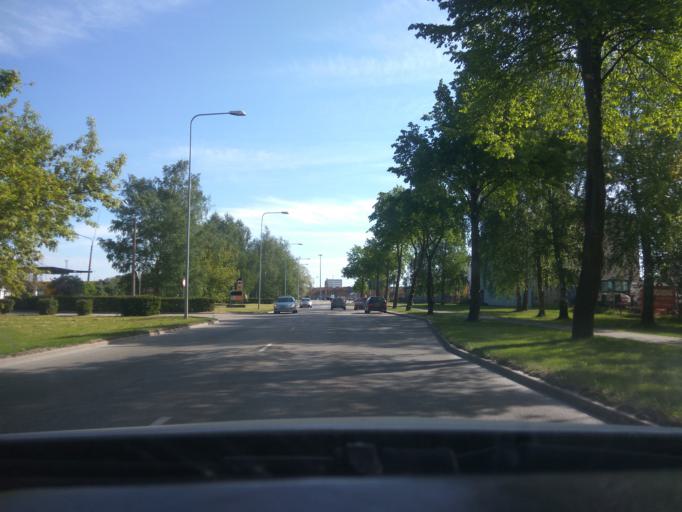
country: LV
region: Ventspils
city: Ventspils
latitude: 57.3837
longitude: 21.5849
